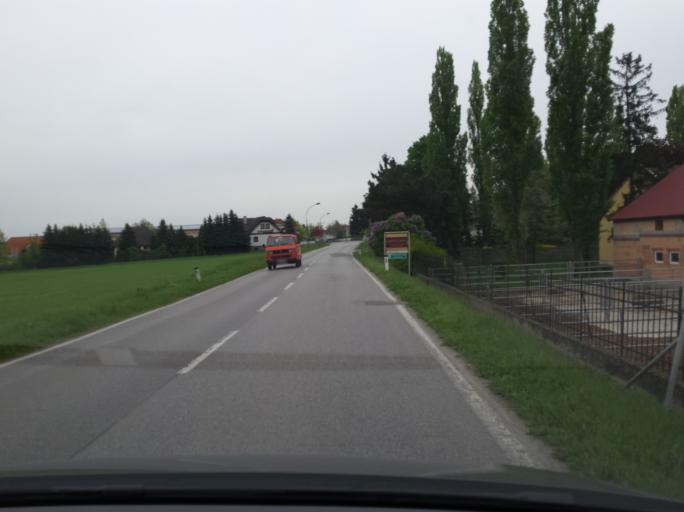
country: AT
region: Lower Austria
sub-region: Politischer Bezirk Bruck an der Leitha
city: Bruck an der Leitha
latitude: 48.0328
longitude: 16.7684
